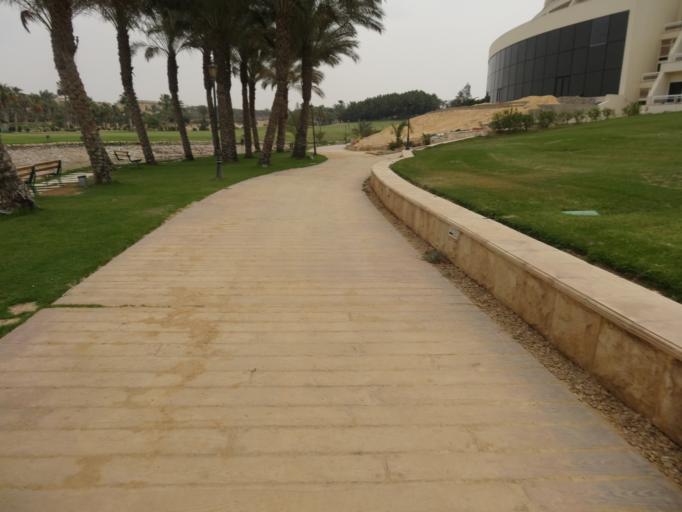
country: EG
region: Muhafazat al Qalyubiyah
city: Al Khankah
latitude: 30.0728
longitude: 31.4350
